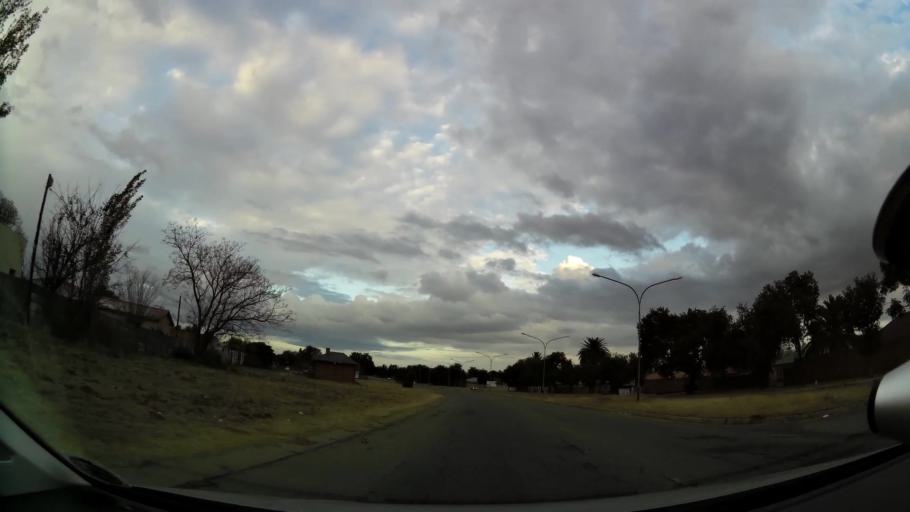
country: ZA
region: Orange Free State
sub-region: Lejweleputswa District Municipality
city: Welkom
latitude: -27.9664
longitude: 26.7410
